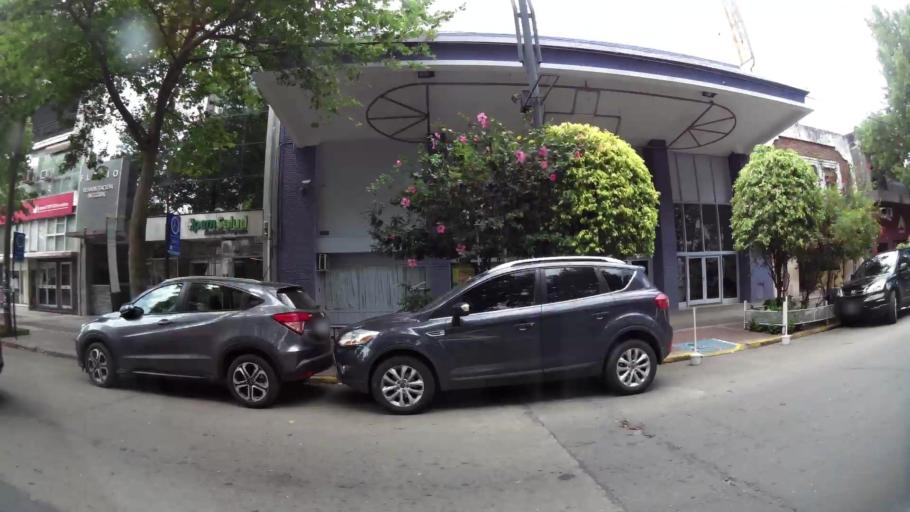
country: AR
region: Santa Fe
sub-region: Departamento de Rosario
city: Rosario
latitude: -32.9751
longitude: -60.6437
